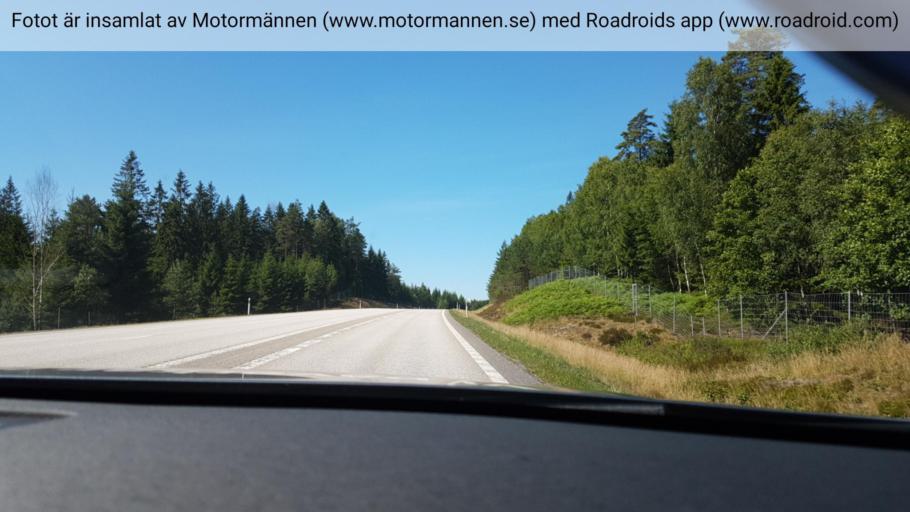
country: SE
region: Vaestra Goetaland
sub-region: Marks Kommun
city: Fritsla
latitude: 57.5441
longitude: 12.8157
